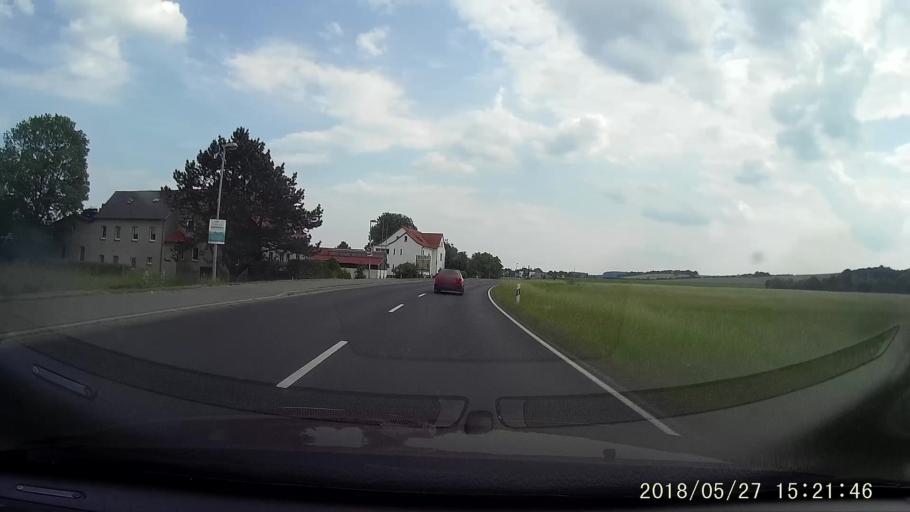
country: DE
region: Saxony
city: Kodersdorf
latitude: 51.2384
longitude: 14.8893
